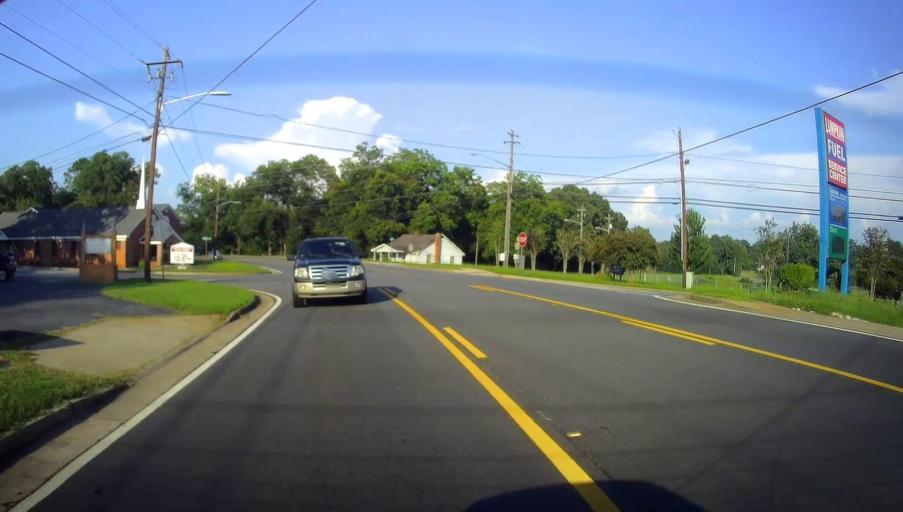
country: US
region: Georgia
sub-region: Houston County
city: Perry
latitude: 32.4631
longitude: -83.7219
